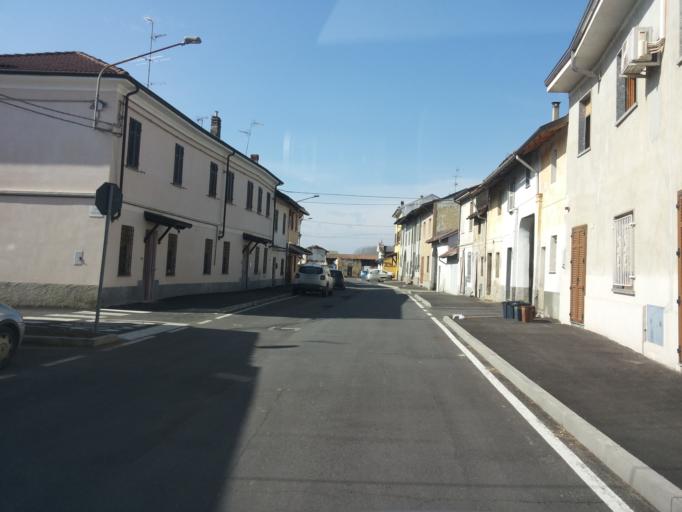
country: IT
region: Piedmont
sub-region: Provincia di Vercelli
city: Asigliano Vercellese
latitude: 45.2601
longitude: 8.4048
